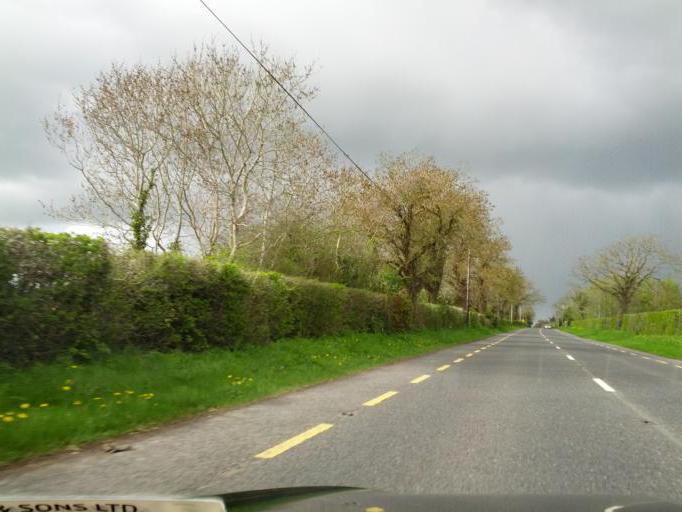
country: IE
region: Leinster
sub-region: An Mhi
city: Dunshaughlin
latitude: 53.5467
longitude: -6.5704
